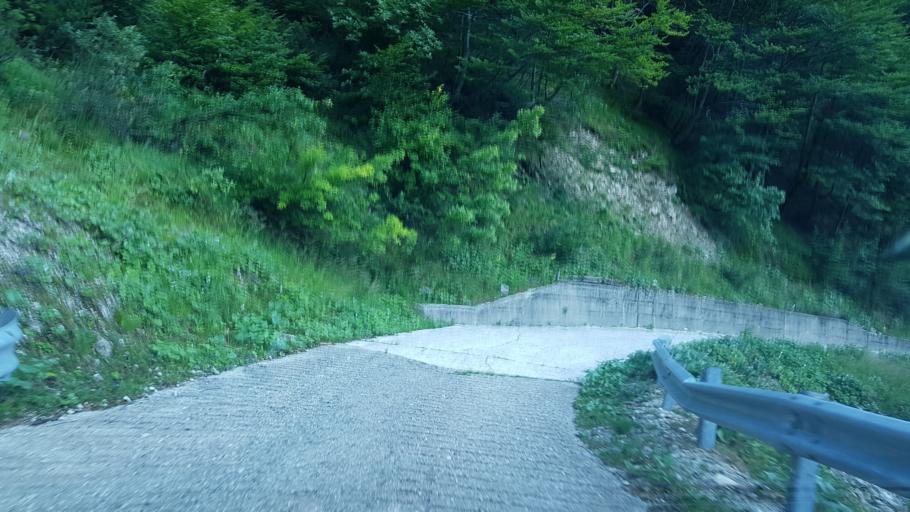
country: IT
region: Friuli Venezia Giulia
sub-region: Provincia di Udine
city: Pontebba
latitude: 46.4814
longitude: 13.2503
